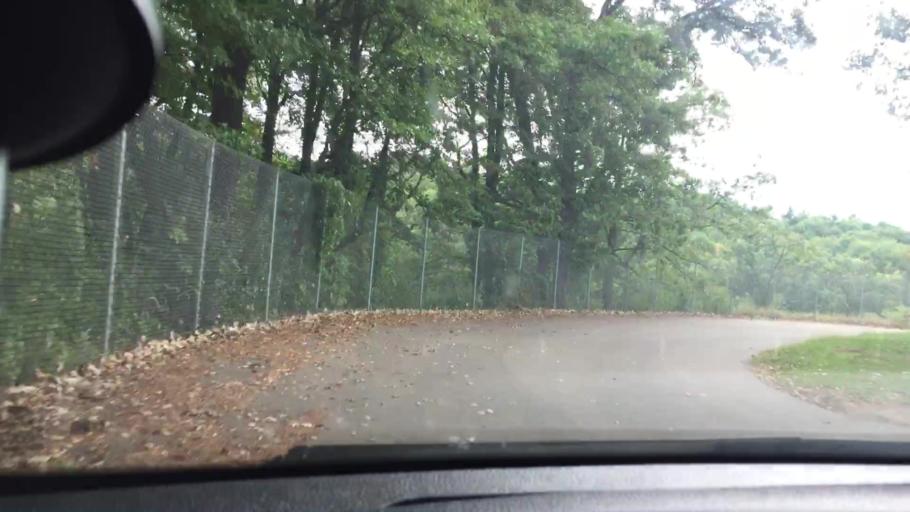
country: US
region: Wisconsin
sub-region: Chippewa County
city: Chippewa Falls
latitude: 44.9523
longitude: -91.4002
